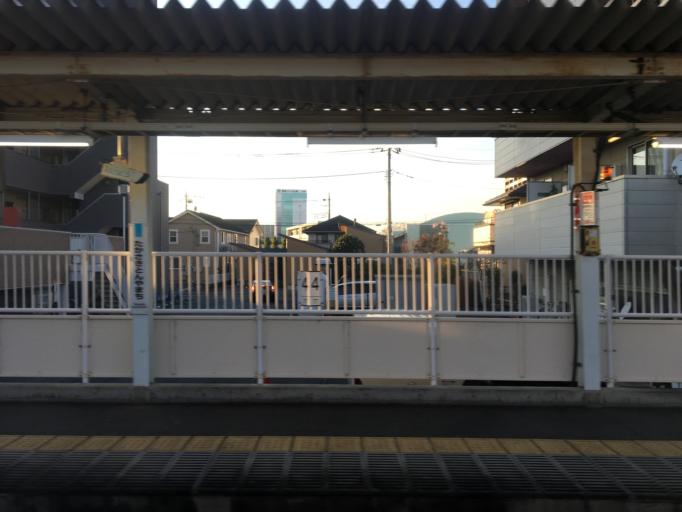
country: JP
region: Gunma
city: Takasaki
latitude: 36.3457
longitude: 139.0170
